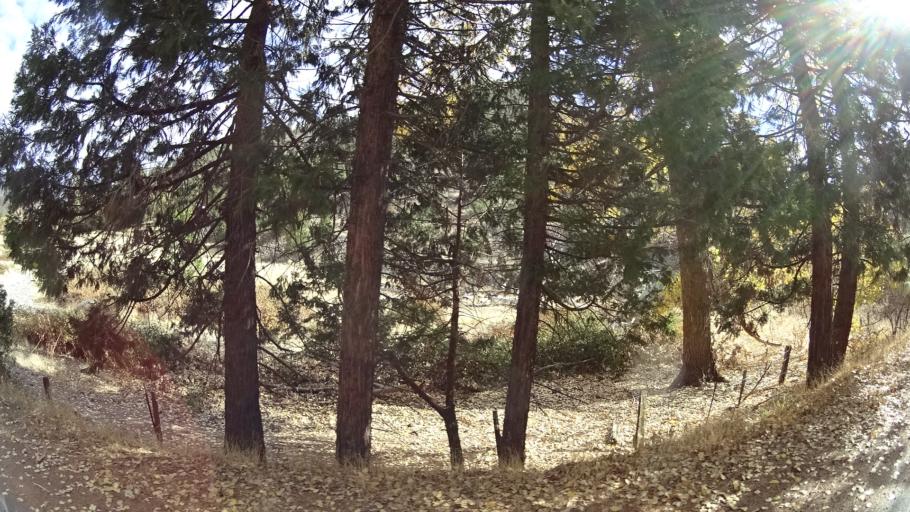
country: US
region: California
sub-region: Siskiyou County
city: Yreka
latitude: 41.6364
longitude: -122.7510
